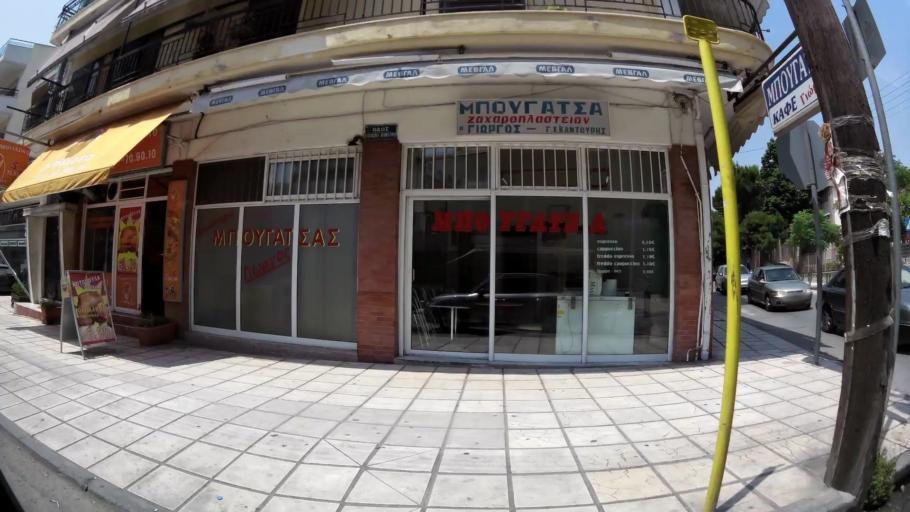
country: GR
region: Central Macedonia
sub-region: Nomos Thessalonikis
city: Evosmos
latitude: 40.6660
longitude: 22.9086
